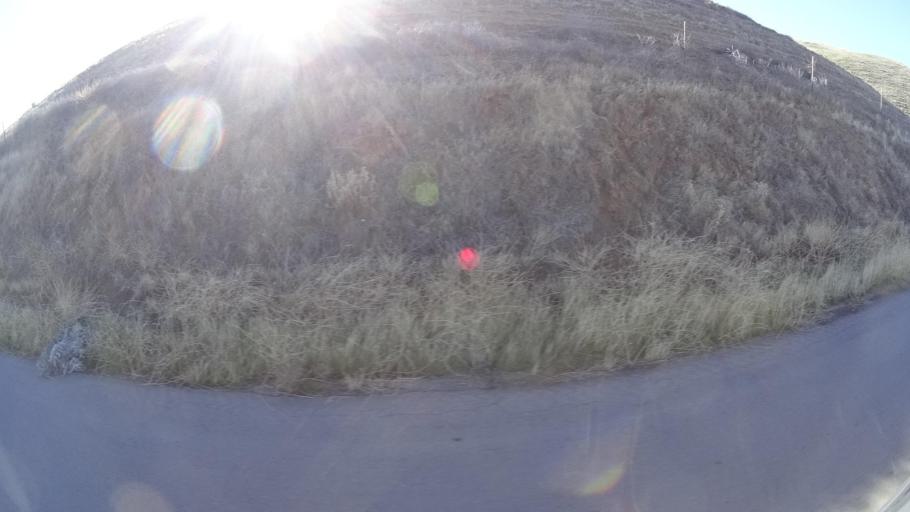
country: US
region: California
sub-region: Kern County
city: Maricopa
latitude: 34.9747
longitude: -119.4607
